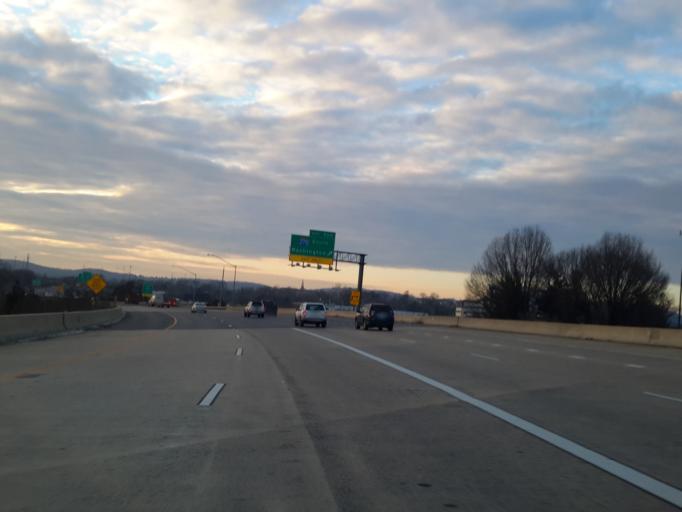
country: US
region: Maryland
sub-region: Frederick County
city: Frederick
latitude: 39.3989
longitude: -77.4254
